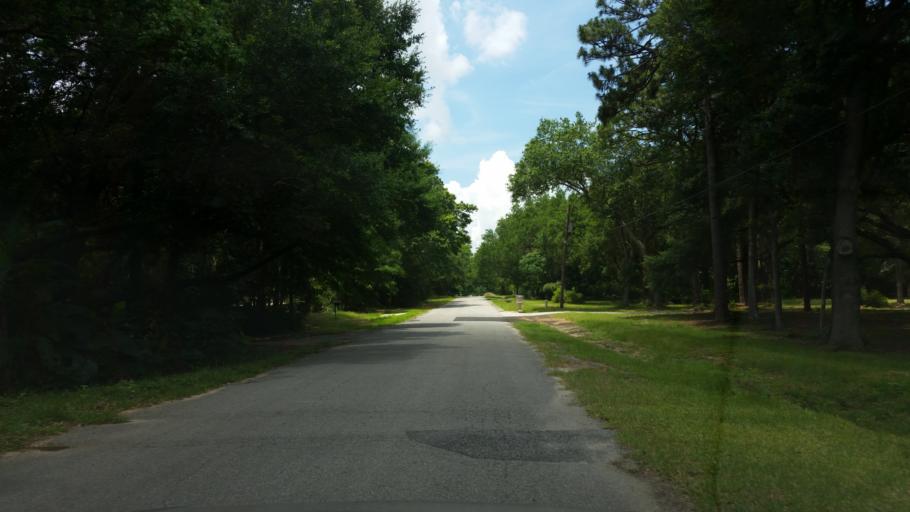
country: US
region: Florida
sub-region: Escambia County
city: Gonzalez
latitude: 30.5467
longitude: -87.3077
